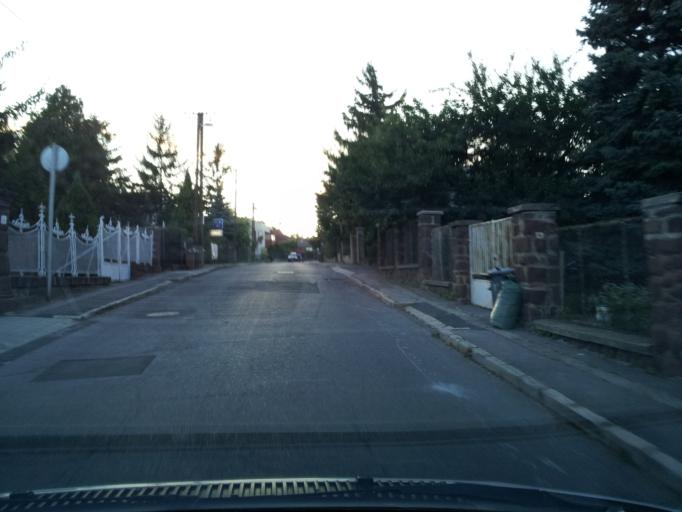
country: HU
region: Veszprem
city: Balatonalmadi
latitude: 47.0324
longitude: 18.0172
